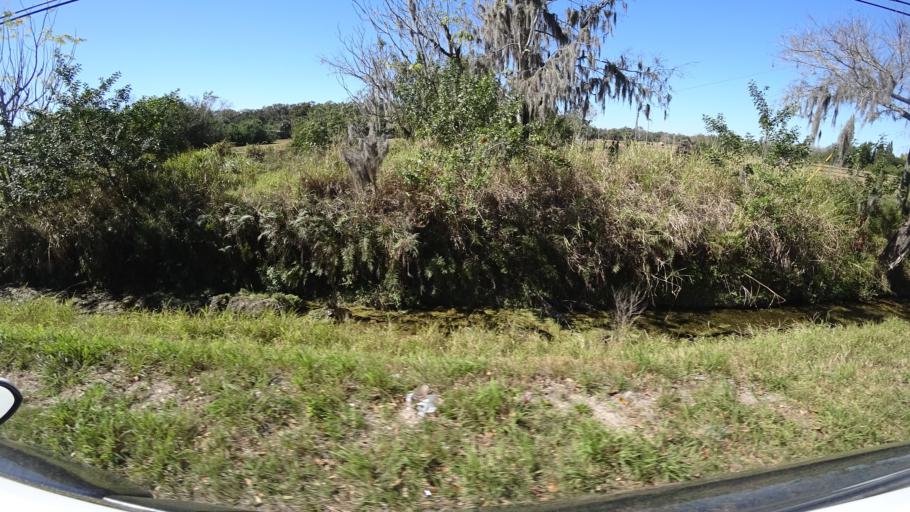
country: US
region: Florida
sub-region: Manatee County
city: Memphis
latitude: 27.5542
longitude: -82.5482
